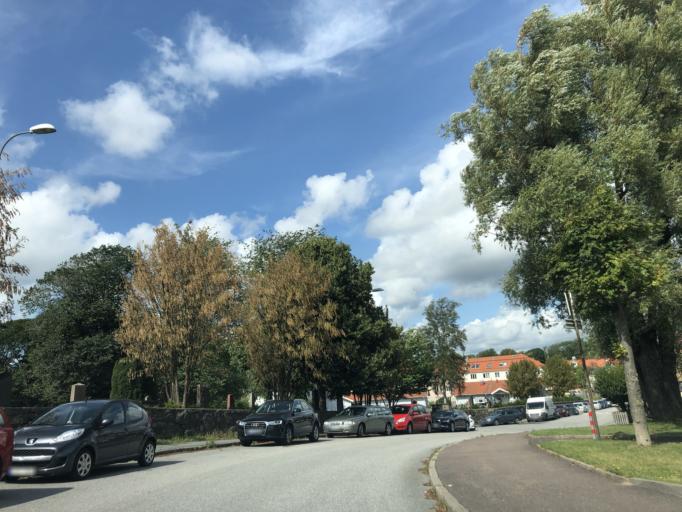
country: SE
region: Vaestra Goetaland
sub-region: Goteborg
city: Majorna
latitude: 57.7072
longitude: 11.9164
